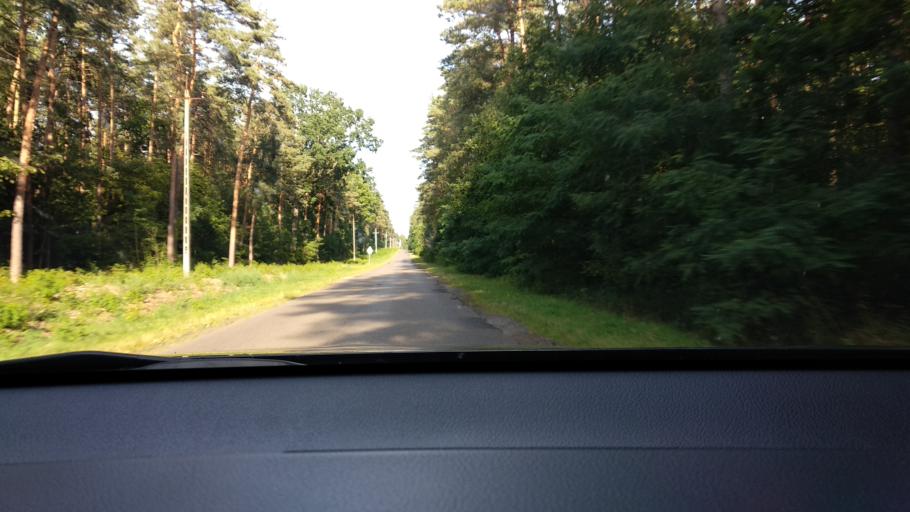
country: PL
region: Masovian Voivodeship
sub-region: Powiat pultuski
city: Pultusk
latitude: 52.7129
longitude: 21.1613
